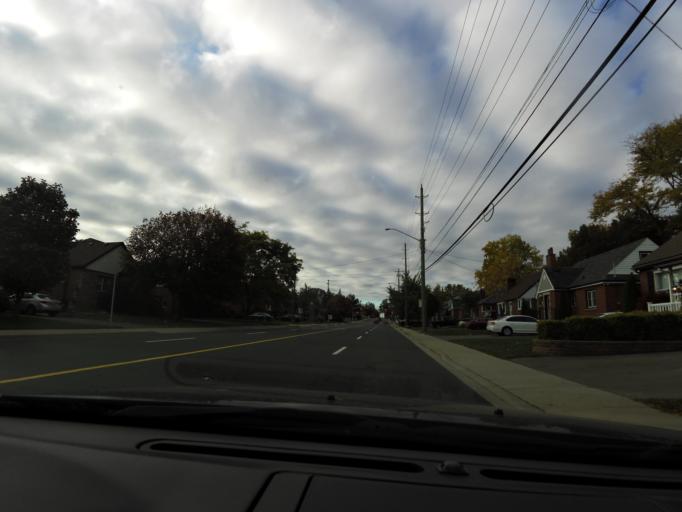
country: CA
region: Ontario
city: Hamilton
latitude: 43.2349
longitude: -79.9001
